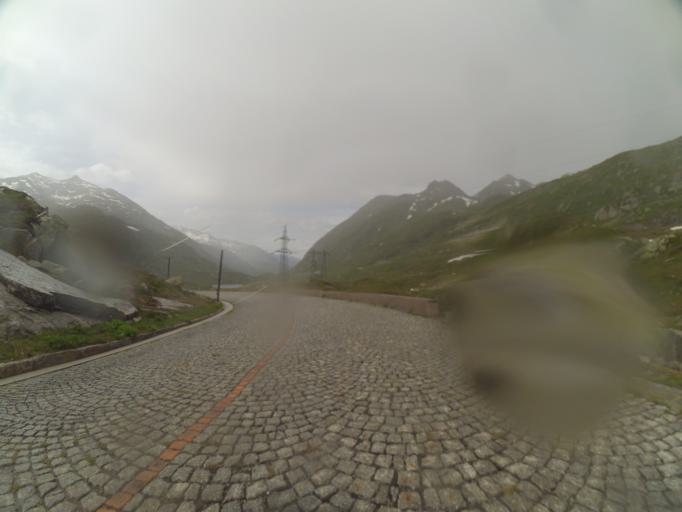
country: CH
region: Ticino
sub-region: Leventina District
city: Airolo
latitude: 46.5641
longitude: 8.5573
